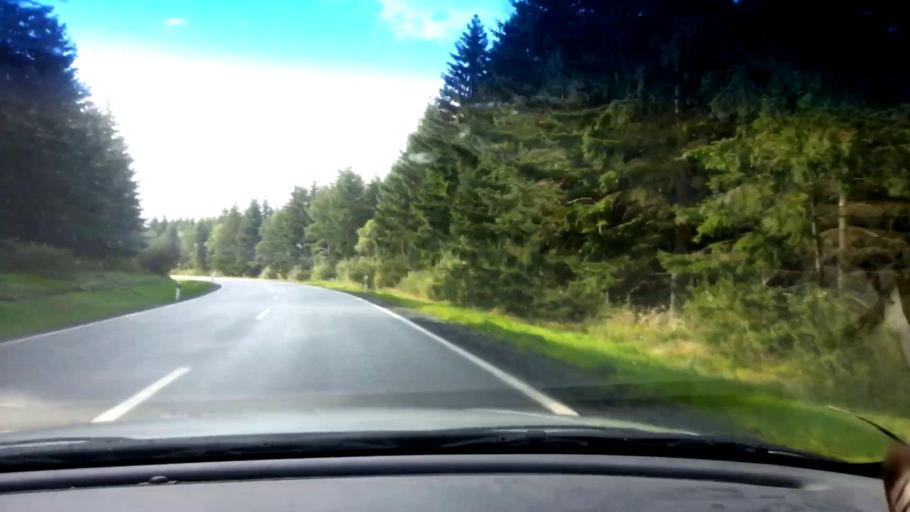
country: DE
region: Bavaria
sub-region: Upper Palatinate
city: Pechbrunn
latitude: 49.9974
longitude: 12.2022
